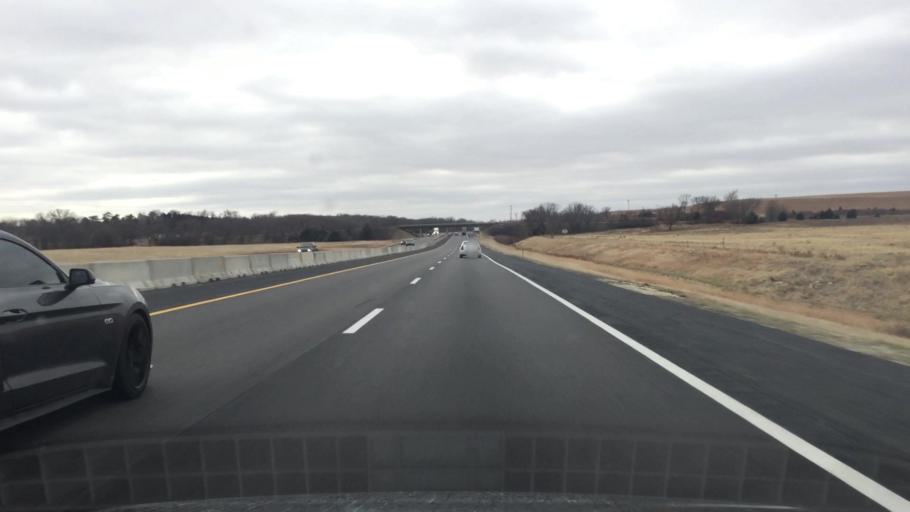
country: US
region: Kansas
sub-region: Chase County
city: Cottonwood Falls
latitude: 38.1269
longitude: -96.5498
